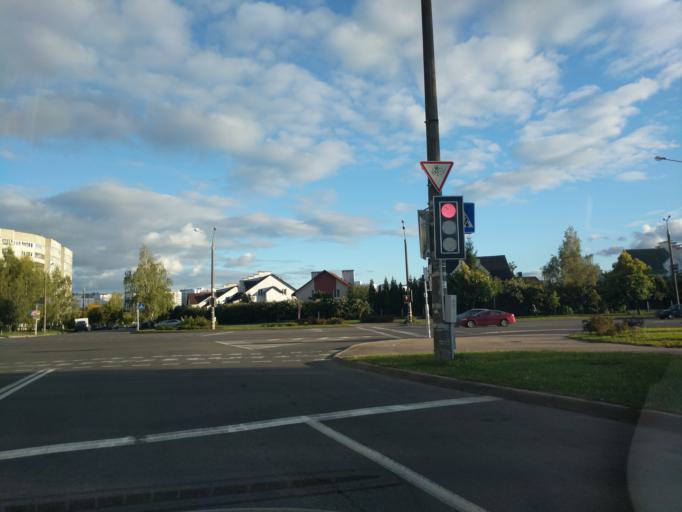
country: BY
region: Minsk
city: Malinovka
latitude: 53.8575
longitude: 27.4555
